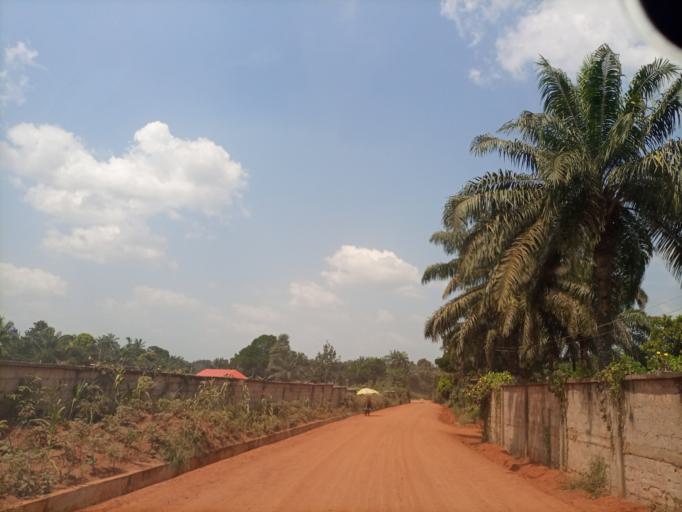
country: NG
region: Enugu
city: Obollo-Afor
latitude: 6.8636
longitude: 7.4740
